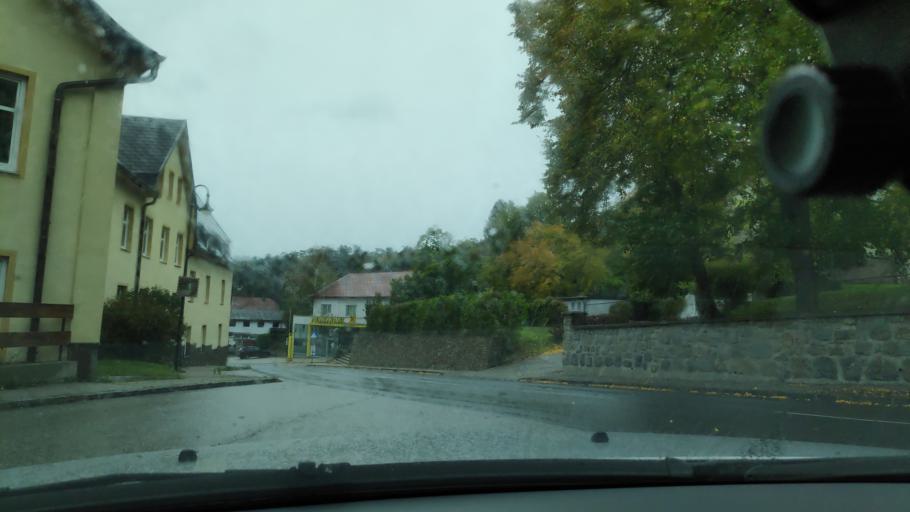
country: AT
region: Lower Austria
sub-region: Politischer Bezirk Neunkirchen
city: Grunbach am Schneeberg
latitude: 47.7980
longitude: 15.9872
